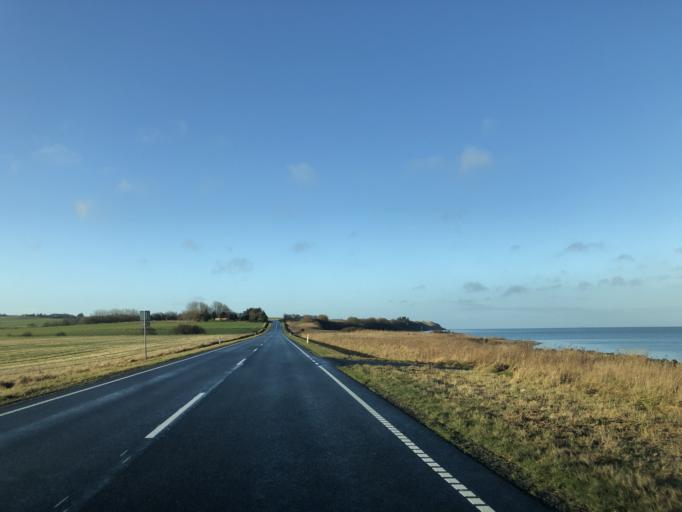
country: DK
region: Central Jutland
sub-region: Struer Kommune
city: Struer
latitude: 56.5581
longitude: 8.4655
